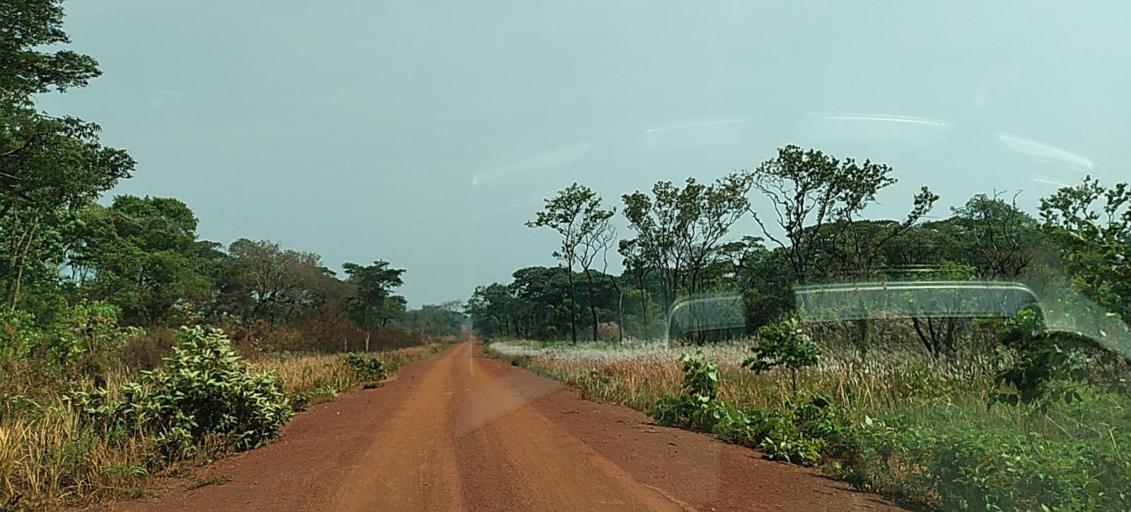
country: ZM
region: North-Western
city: Kansanshi
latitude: -12.0205
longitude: 26.8496
